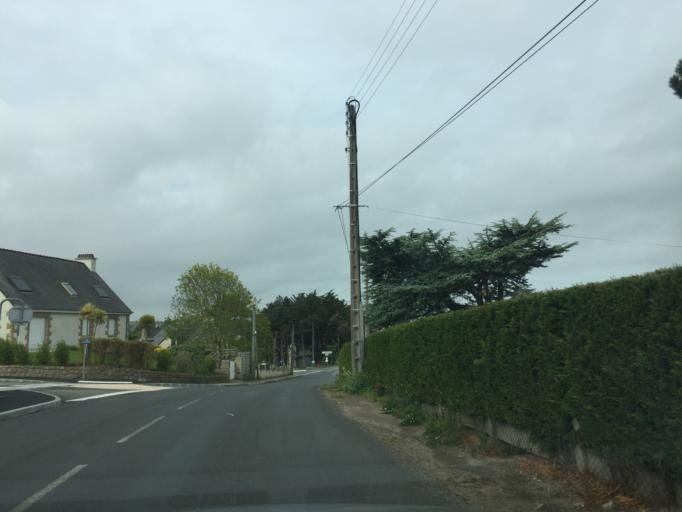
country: FR
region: Brittany
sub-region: Departement des Cotes-d'Armor
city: Saint-Cast-le-Guildo
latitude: 48.6424
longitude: -2.2481
